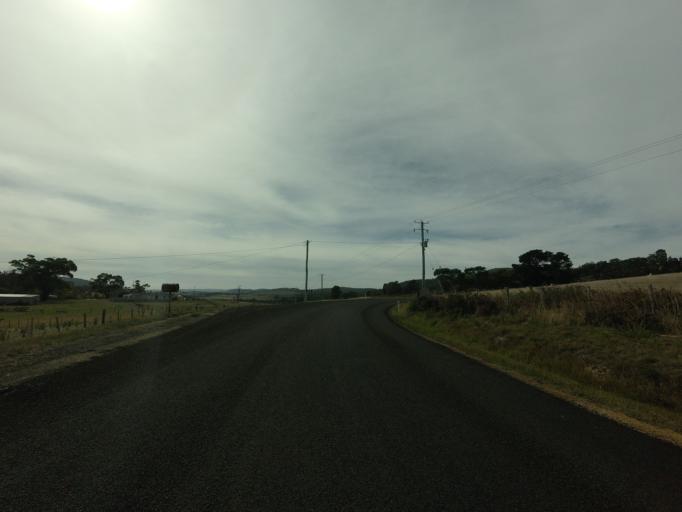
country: AU
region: Tasmania
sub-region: Sorell
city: Sorell
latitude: -42.4265
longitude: 147.4947
